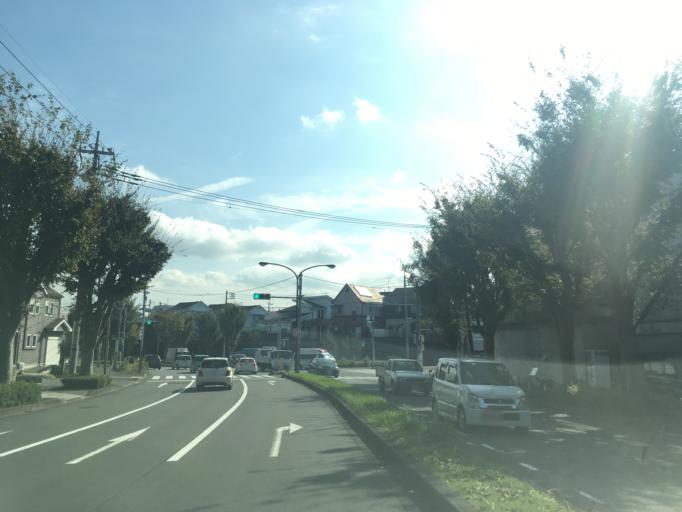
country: JP
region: Tokyo
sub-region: Machida-shi
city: Machida
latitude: 35.5798
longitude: 139.4122
